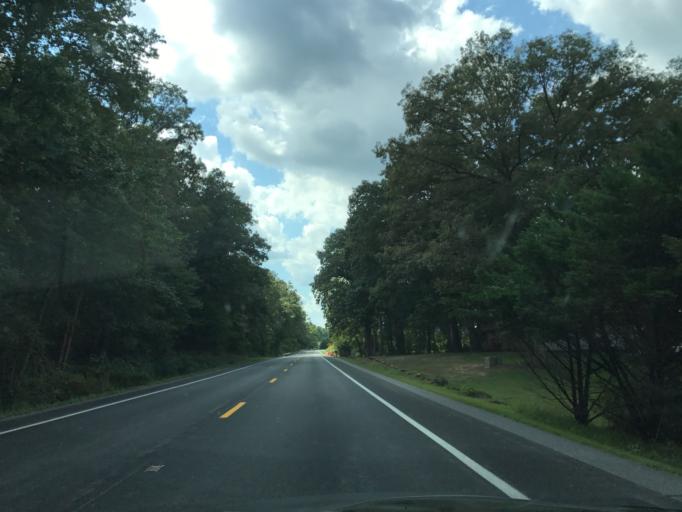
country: US
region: Maryland
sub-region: Queen Anne's County
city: Kingstown
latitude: 39.1440
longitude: -75.9012
